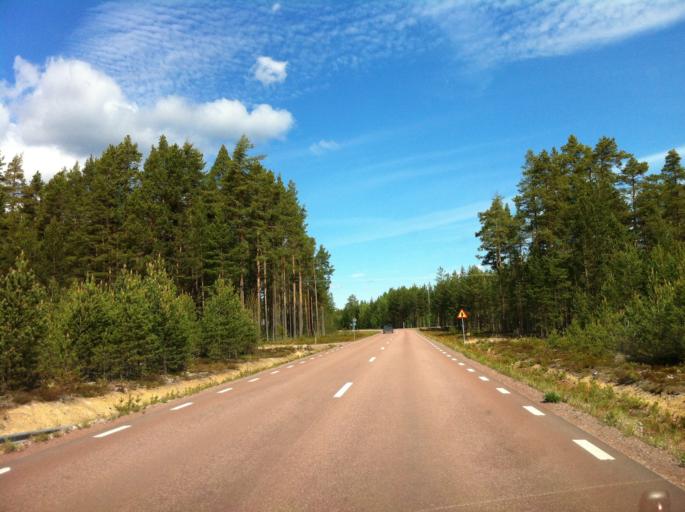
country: SE
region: Dalarna
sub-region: Mora Kommun
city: Mora
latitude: 60.9635
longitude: 14.5212
